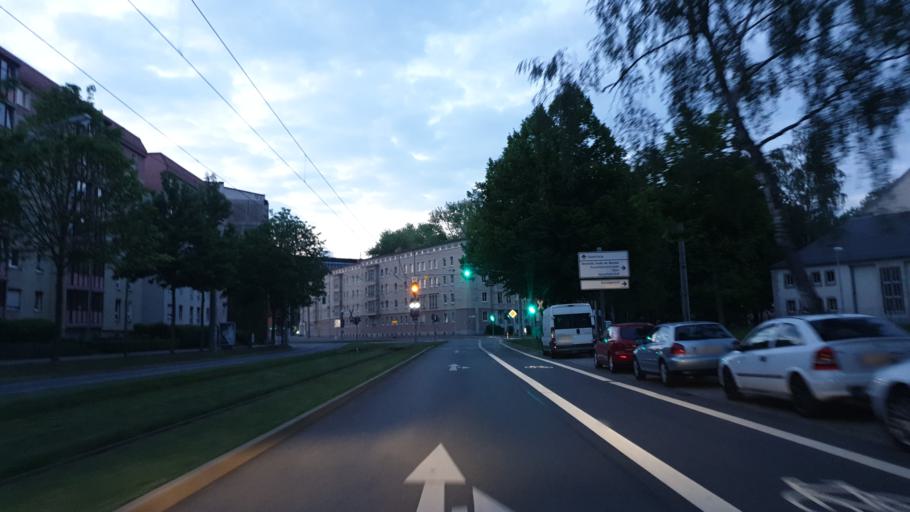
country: DE
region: Saxony
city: Chemnitz
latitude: 50.8274
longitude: 12.9205
